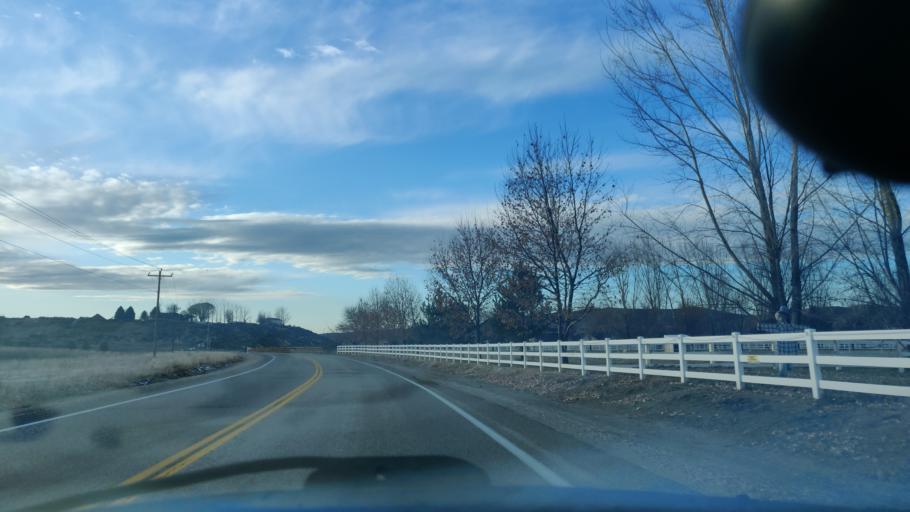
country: US
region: Idaho
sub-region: Ada County
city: Eagle
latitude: 43.7298
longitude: -116.2646
